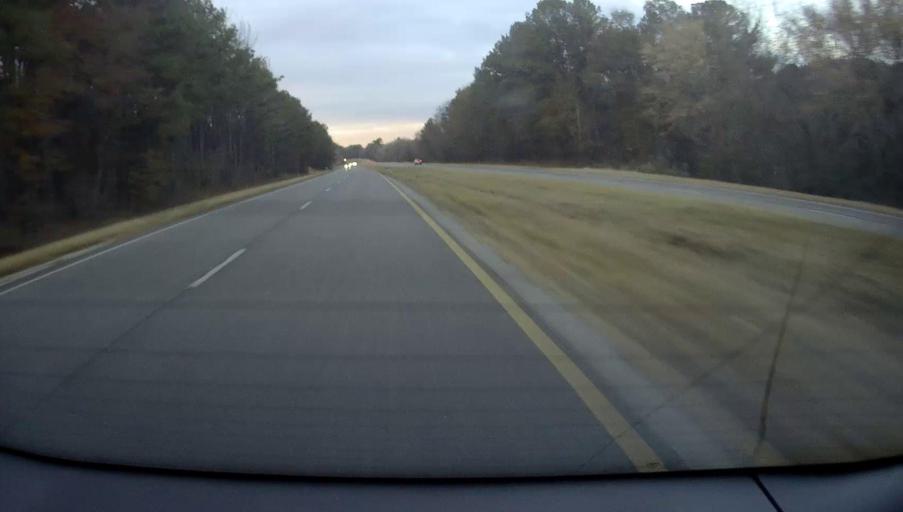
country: US
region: Alabama
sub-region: Etowah County
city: Glencoe
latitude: 33.9264
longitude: -85.9135
